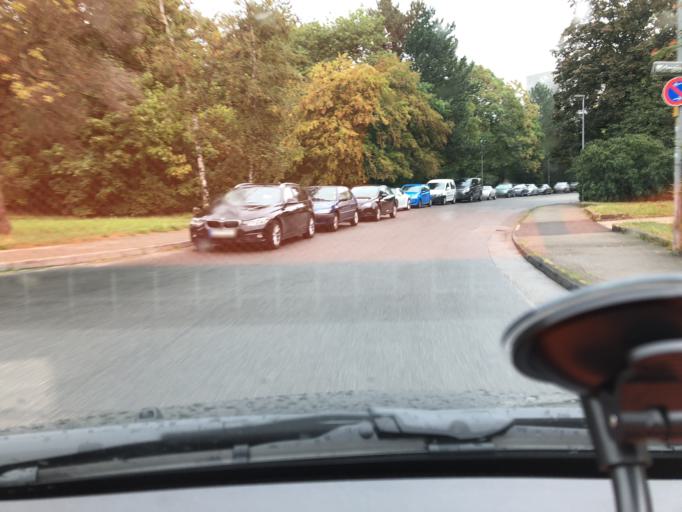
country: DE
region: Baden-Wuerttemberg
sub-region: Regierungsbezirk Stuttgart
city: Leinfelden-Echterdingen
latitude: 48.7237
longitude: 9.1567
